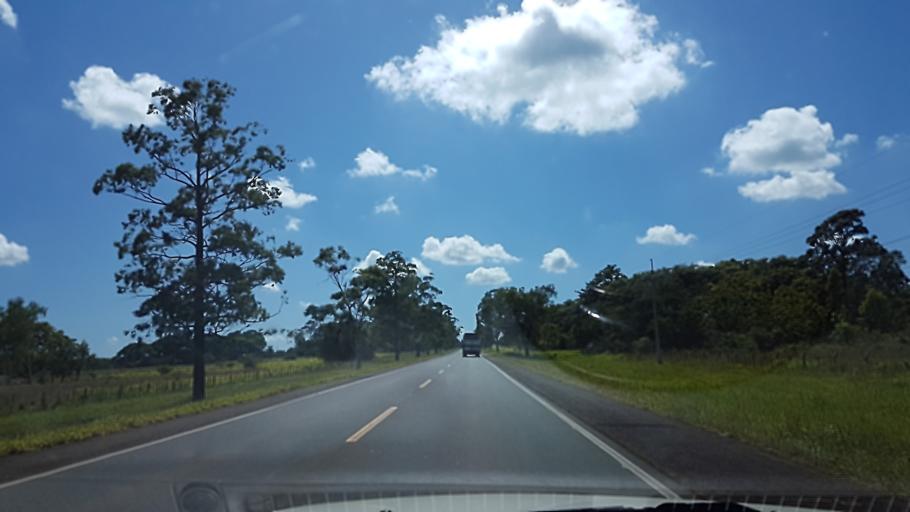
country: PY
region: Itapua
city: Carmen del Parana
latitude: -27.2214
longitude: -56.1148
